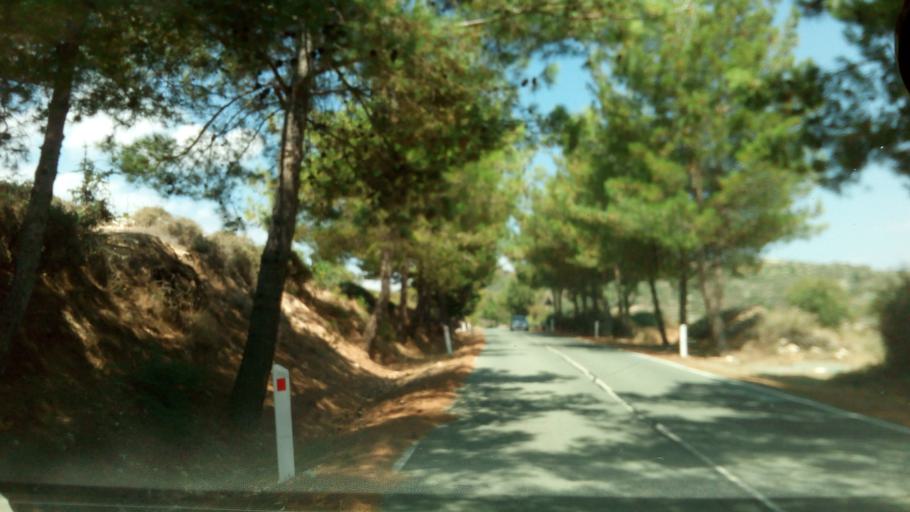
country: CY
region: Limassol
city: Pachna
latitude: 34.8344
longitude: 32.8541
